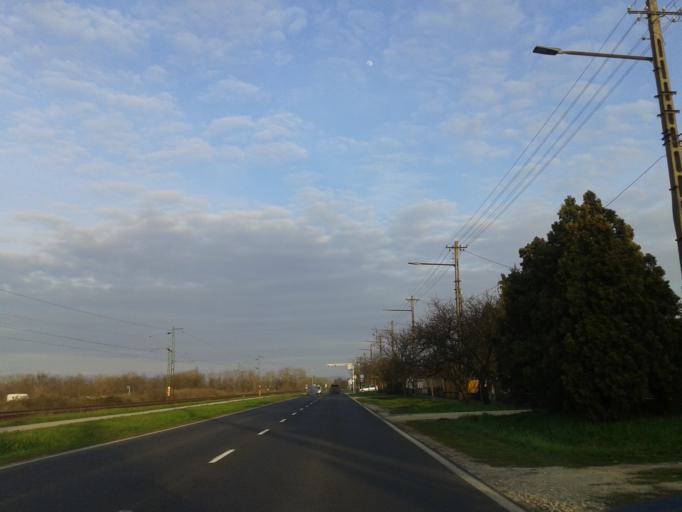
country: HU
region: Komarom-Esztergom
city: Mocsa
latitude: 47.7345
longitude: 18.1884
